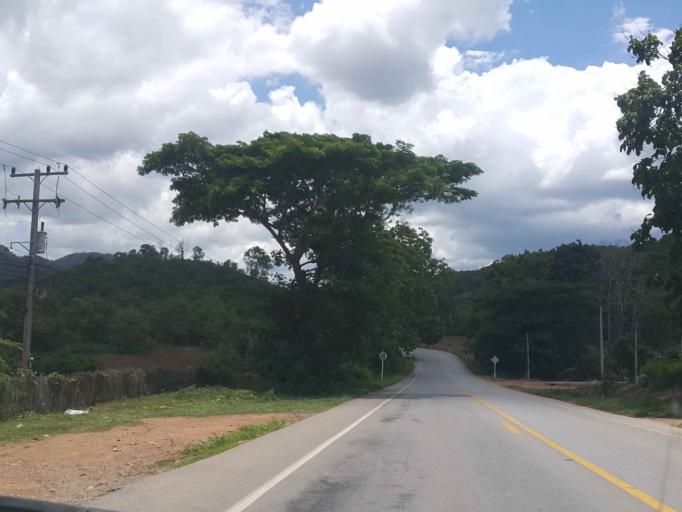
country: TH
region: Nan
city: Wiang Sa
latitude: 18.5221
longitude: 100.5575
